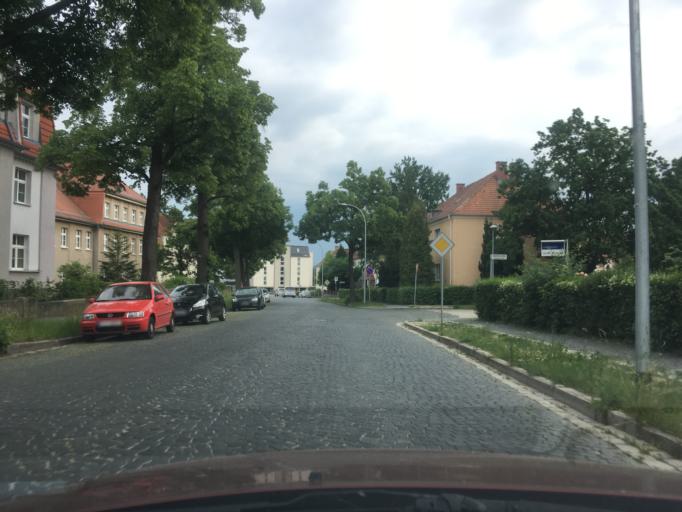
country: DE
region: Saxony
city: Bautzen
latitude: 51.1750
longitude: 14.4446
